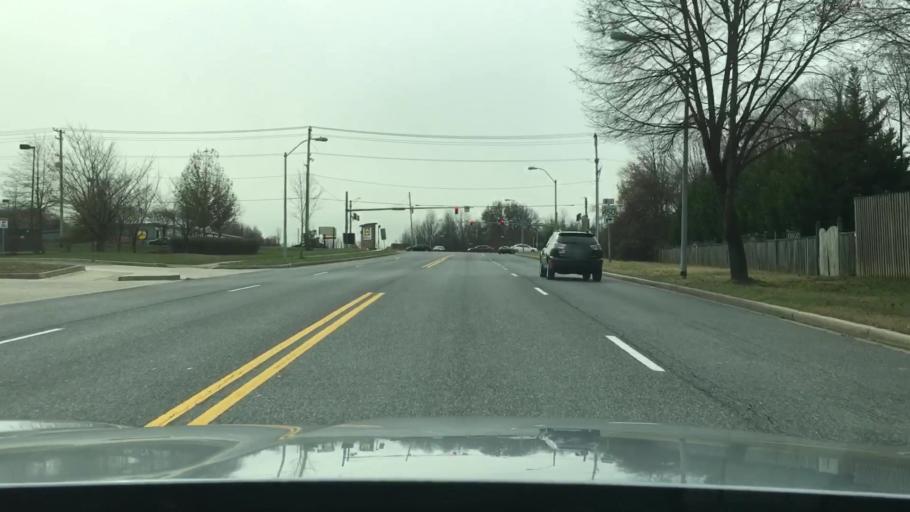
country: US
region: Maryland
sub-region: Prince George's County
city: Glenn Dale
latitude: 38.9735
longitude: -76.7732
